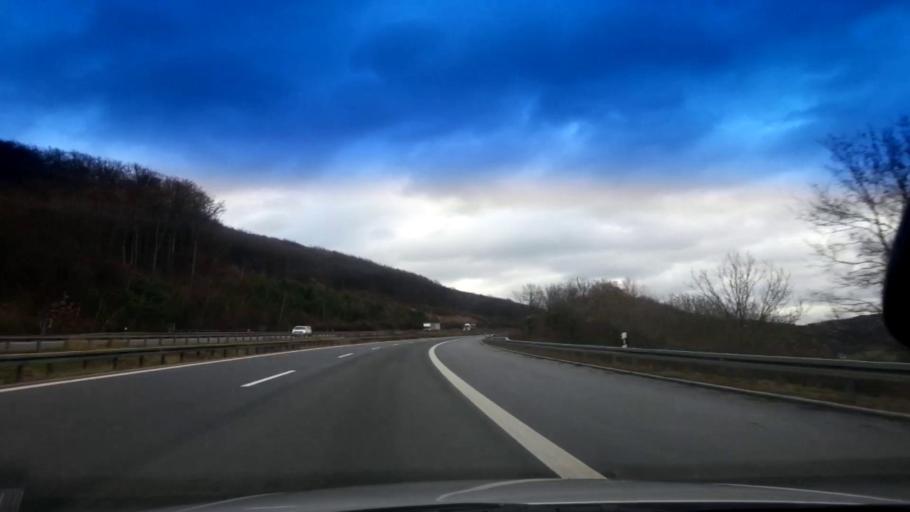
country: DE
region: Bavaria
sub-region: Upper Franconia
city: Schesslitz
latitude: 49.9840
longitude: 11.0759
